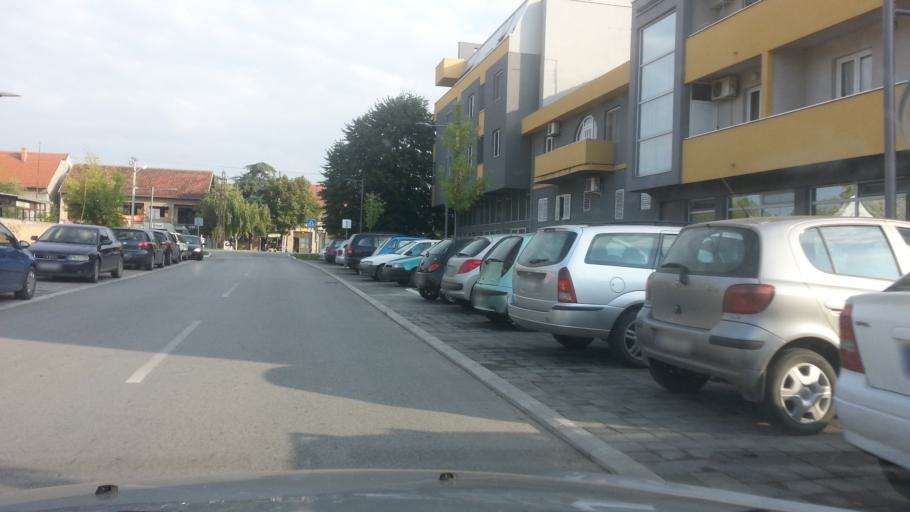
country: RS
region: Autonomna Pokrajina Vojvodina
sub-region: Sremski Okrug
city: Stara Pazova
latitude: 44.9836
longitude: 20.1559
